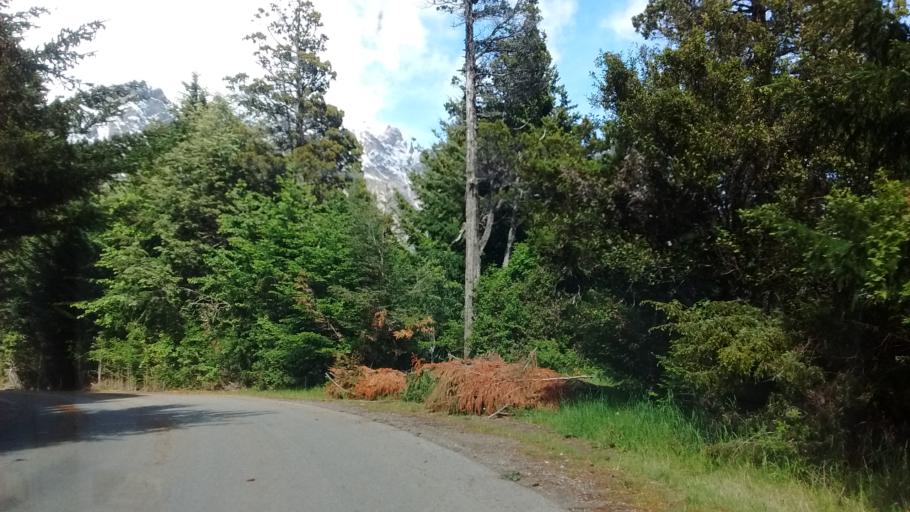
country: AR
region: Rio Negro
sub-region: Departamento de Bariloche
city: San Carlos de Bariloche
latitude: -41.0714
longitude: -71.5443
